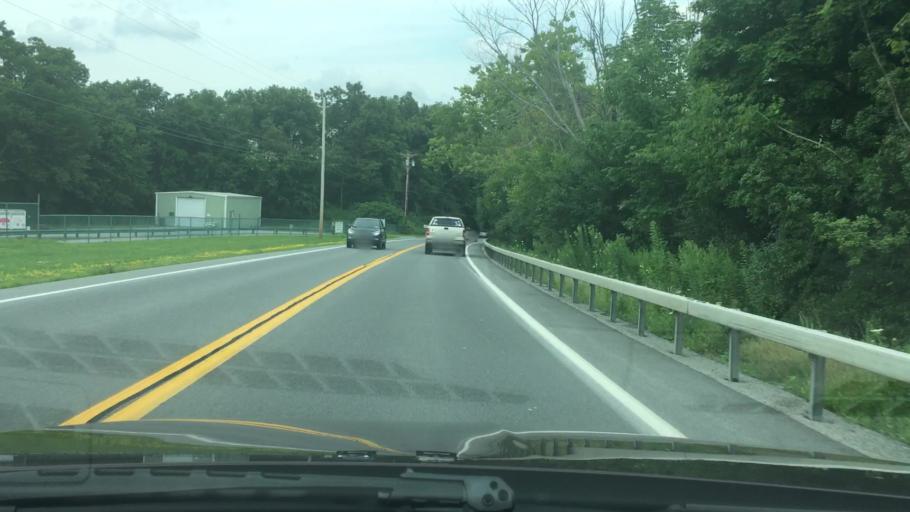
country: US
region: New York
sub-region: Dutchess County
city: Hillside Lake
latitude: 41.6480
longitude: -73.7269
